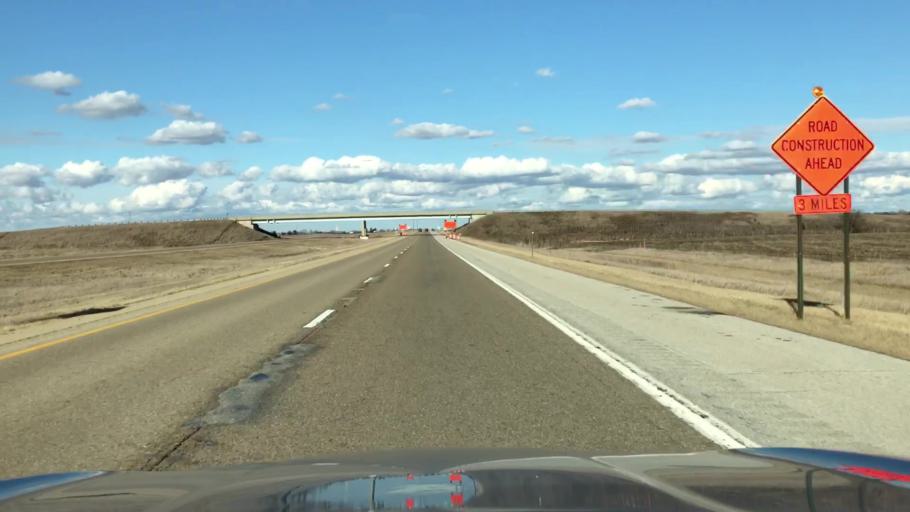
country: US
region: Illinois
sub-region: McLean County
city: Chenoa
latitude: 40.7246
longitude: -88.7370
